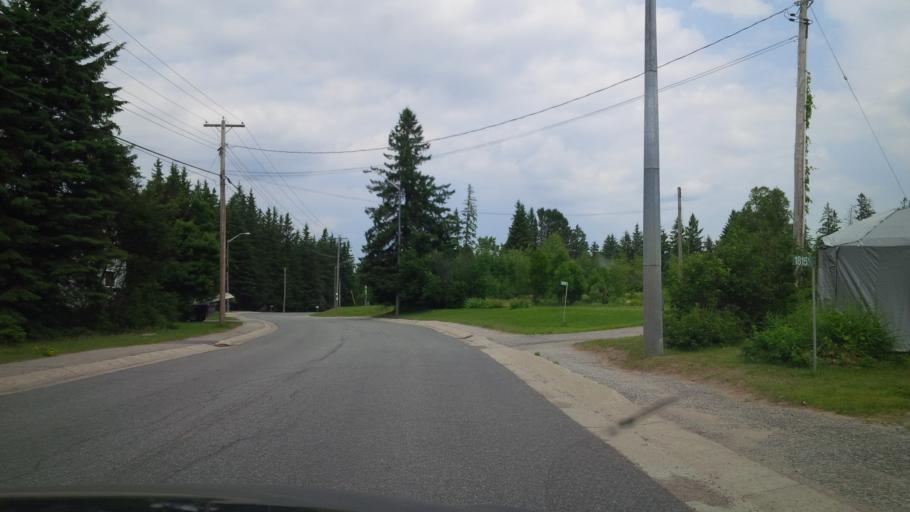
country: CA
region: Ontario
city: Huntsville
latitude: 45.5605
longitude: -79.2280
